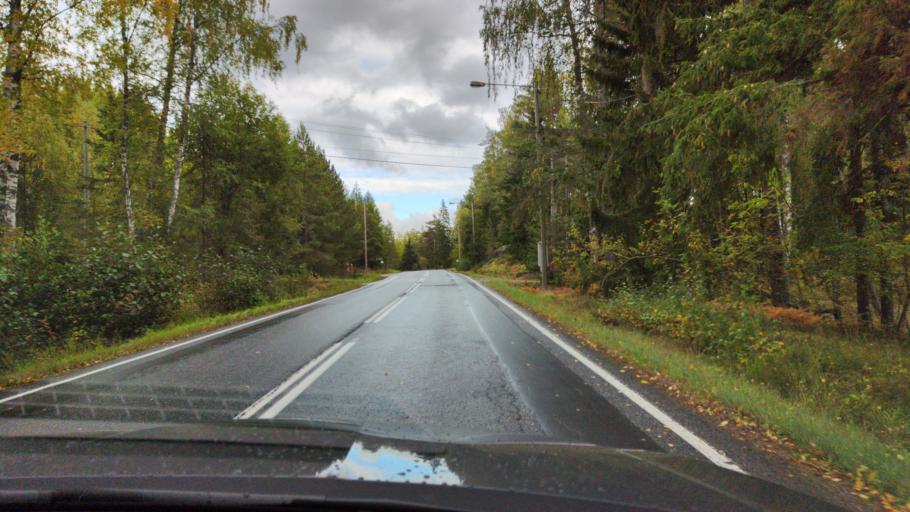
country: FI
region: Varsinais-Suomi
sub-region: Aboland-Turunmaa
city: Pargas
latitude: 60.3710
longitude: 22.2619
